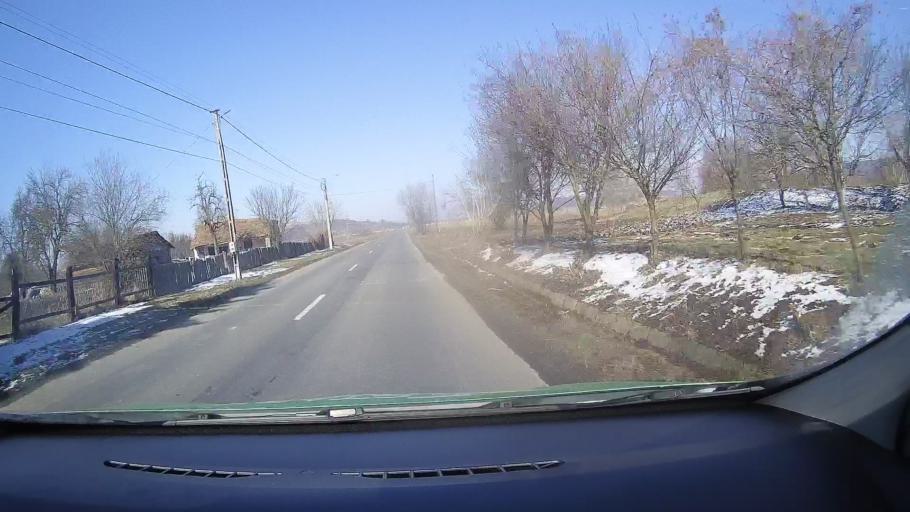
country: RO
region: Brasov
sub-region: Comuna Homorod
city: Homorod
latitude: 46.0224
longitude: 25.2743
